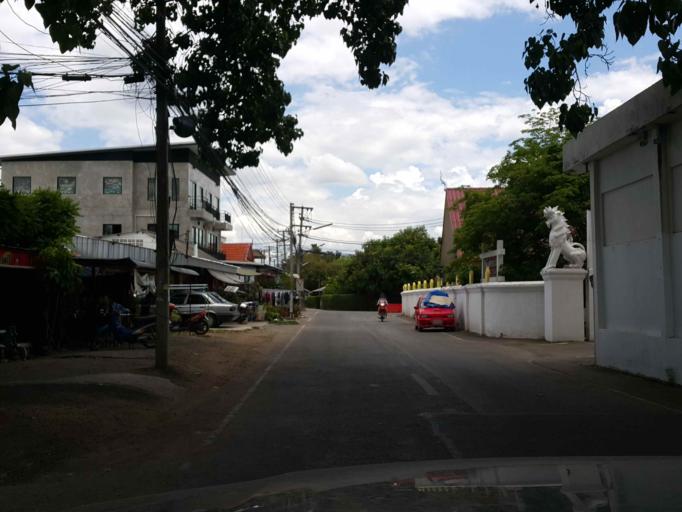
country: TH
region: Chiang Mai
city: Chiang Mai
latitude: 18.7662
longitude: 99.0125
